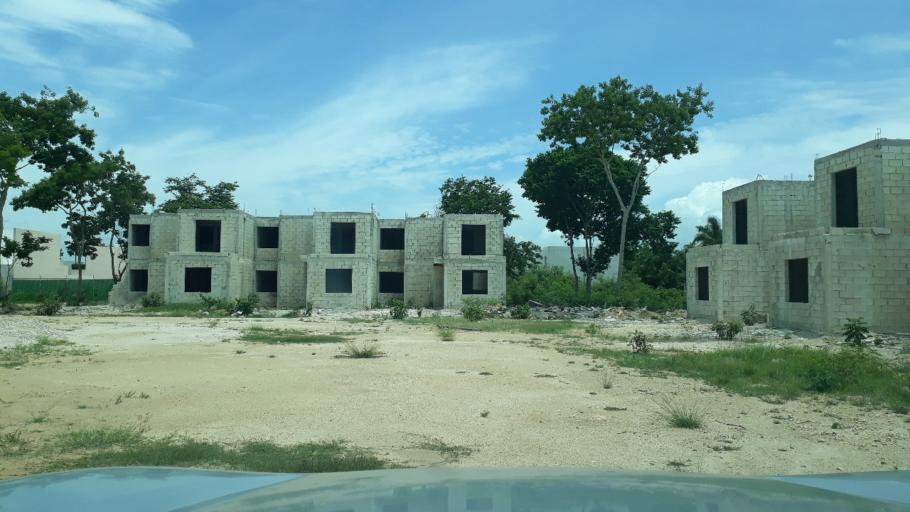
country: MX
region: Quintana Roo
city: Calderitas
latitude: 18.5594
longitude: -88.2562
